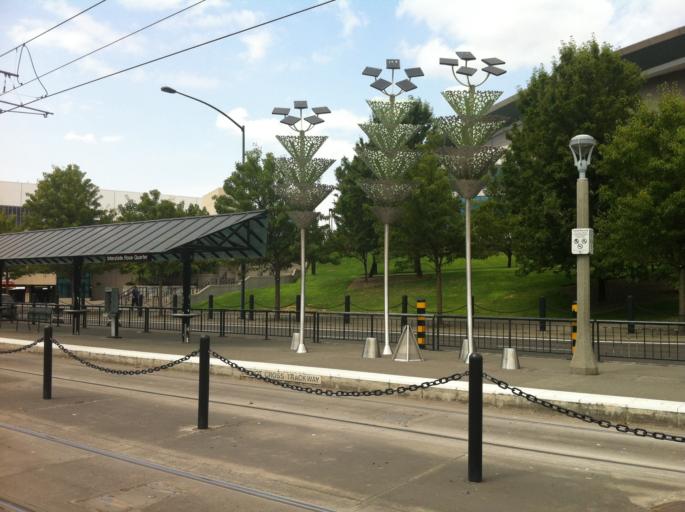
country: US
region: Oregon
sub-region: Multnomah County
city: Portland
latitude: 45.5301
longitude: -122.6676
